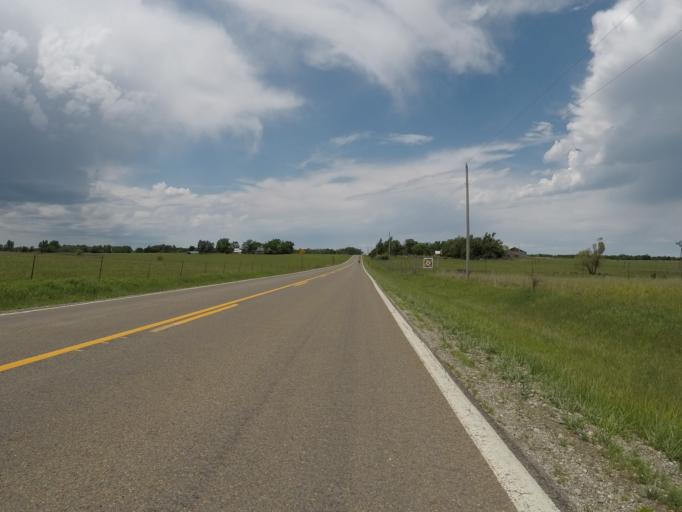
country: US
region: Kansas
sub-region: Morris County
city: Council Grove
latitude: 38.8546
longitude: -96.4221
